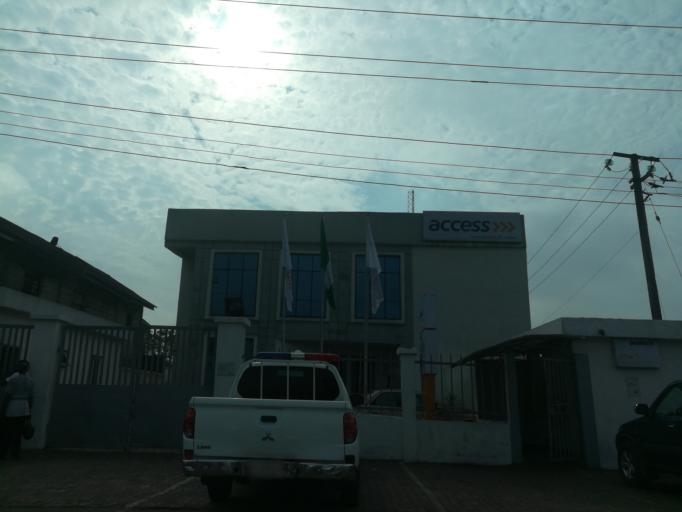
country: NG
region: Rivers
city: Port Harcourt
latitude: 4.8011
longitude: 6.9953
